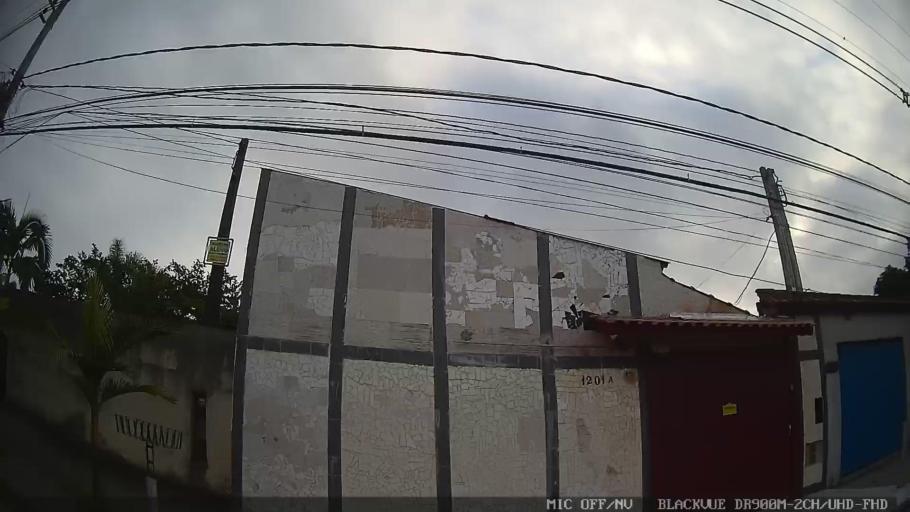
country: BR
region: Sao Paulo
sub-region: Guaruja
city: Guaruja
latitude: -23.9746
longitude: -46.2102
